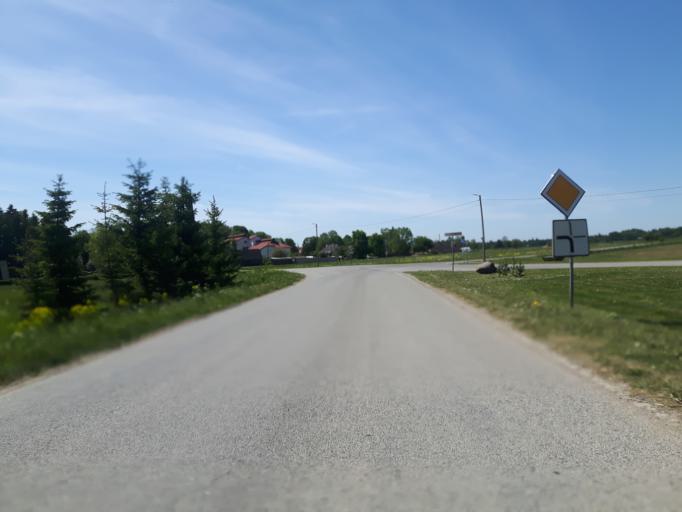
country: EE
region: Laeaene-Virumaa
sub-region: Viru-Nigula vald
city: Kunda
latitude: 59.4492
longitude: 26.6915
